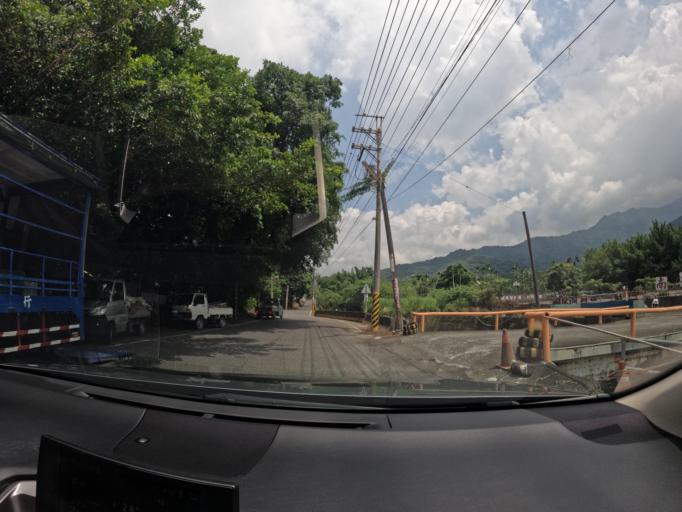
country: TW
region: Taiwan
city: Lugu
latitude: 23.8088
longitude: 120.8308
